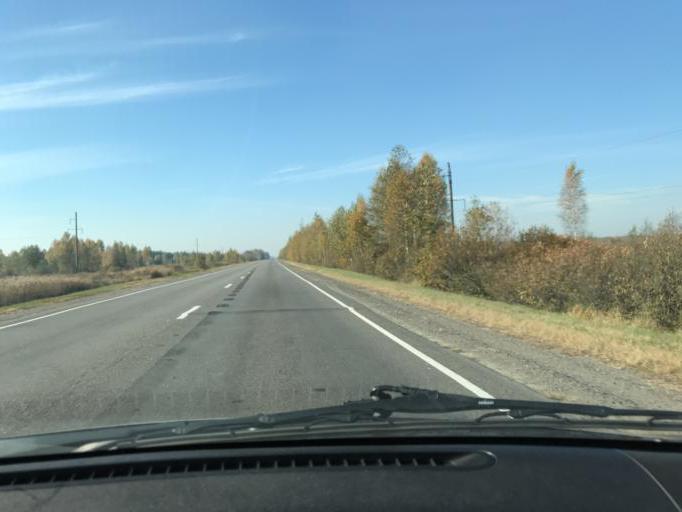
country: BY
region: Brest
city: Horad Luninyets
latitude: 52.3144
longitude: 26.5585
